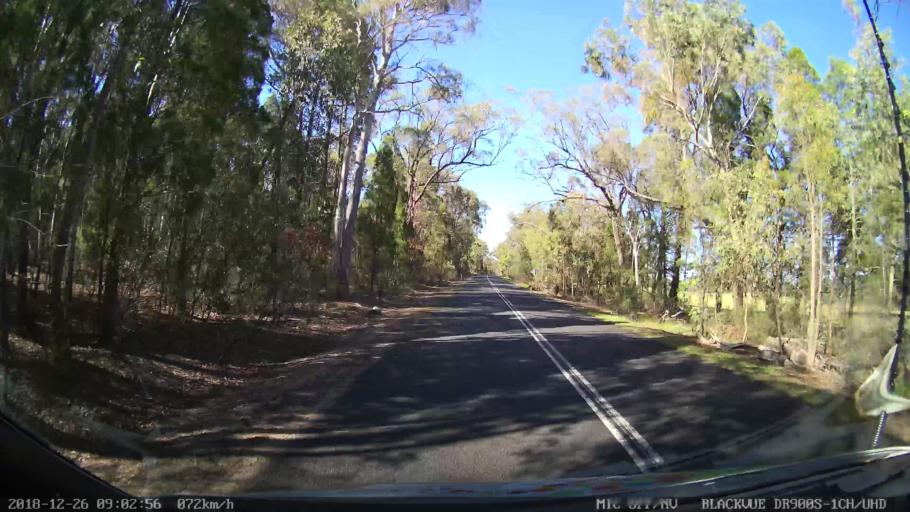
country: AU
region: New South Wales
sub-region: Mid-Western Regional
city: Kandos
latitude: -32.6577
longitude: 150.0163
